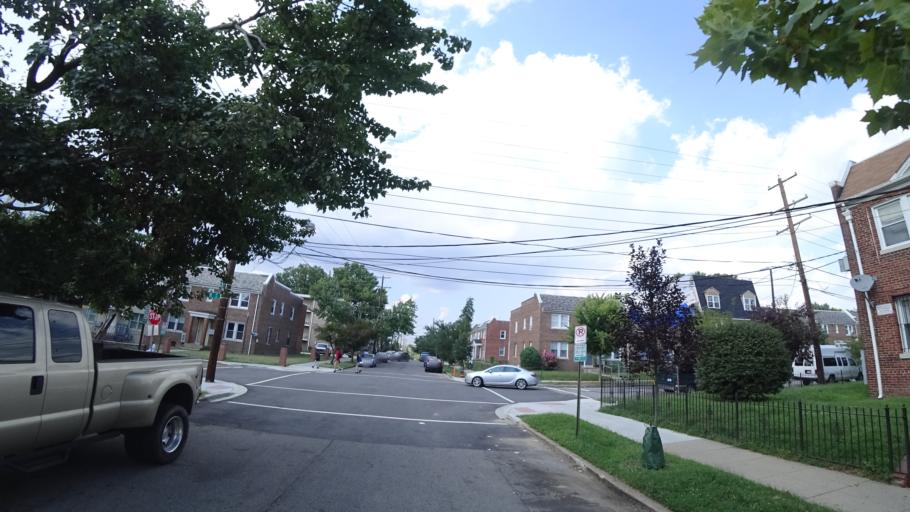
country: US
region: Maryland
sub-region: Prince George's County
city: Hillcrest Heights
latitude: 38.8693
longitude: -76.9808
